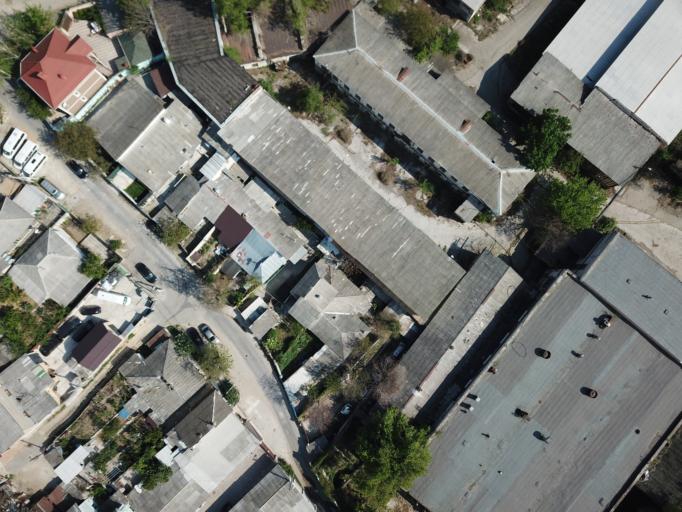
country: MD
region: Chisinau
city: Chisinau
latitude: 47.0116
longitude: 28.8518
